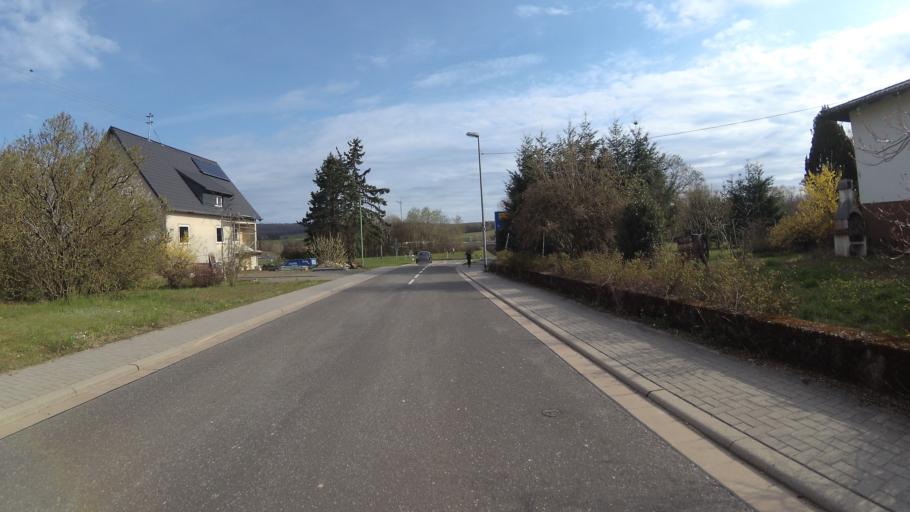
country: DE
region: Rheinland-Pfalz
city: Reichweiler
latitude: 49.5396
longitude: 7.2927
